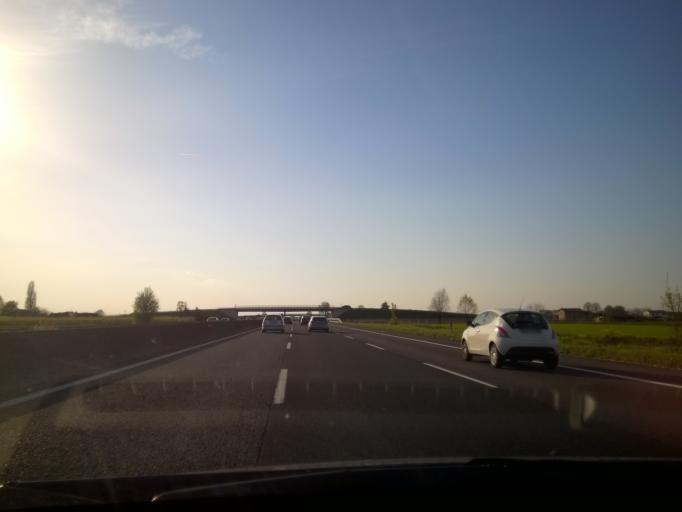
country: IT
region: Emilia-Romagna
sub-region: Provincia di Bologna
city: Castel Guelfo di Bologna
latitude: 44.3994
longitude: 11.6941
